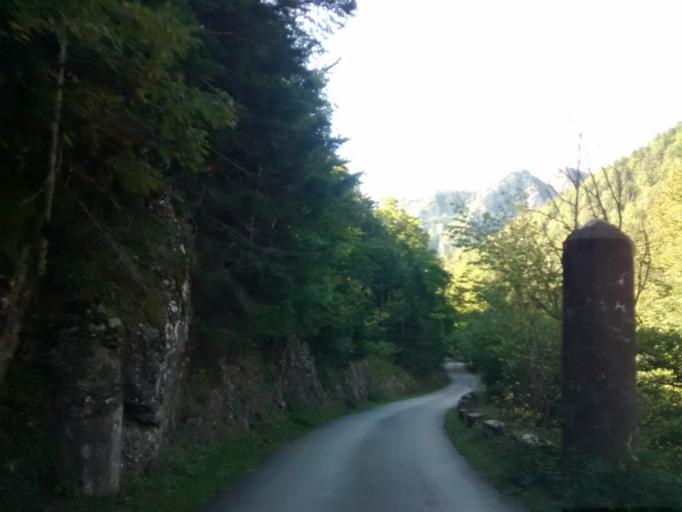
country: ES
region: Aragon
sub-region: Provincia de Huesca
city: Aragues del Puerto
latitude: 42.8468
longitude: -0.7084
